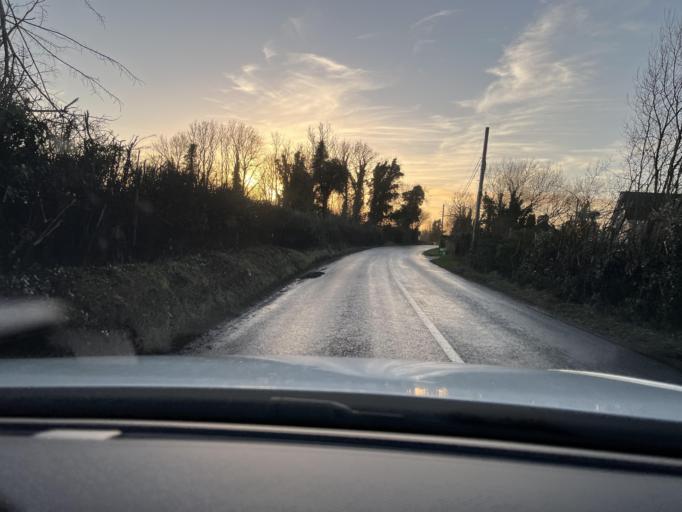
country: IE
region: Ulster
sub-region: An Cabhan
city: Ballyconnell
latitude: 54.0870
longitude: -7.6483
